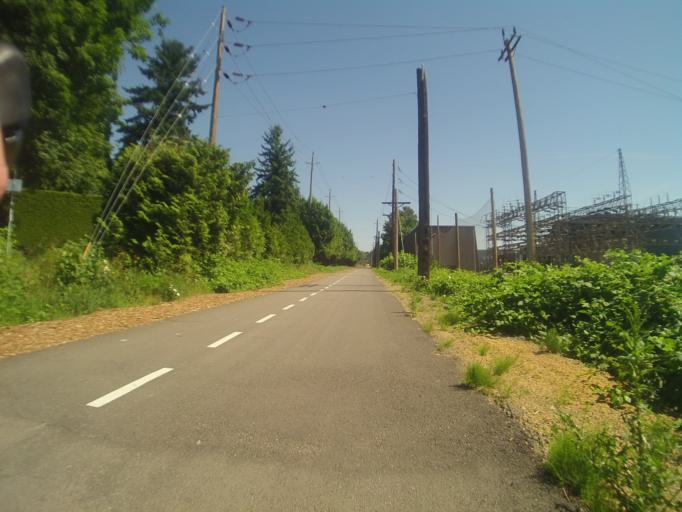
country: CA
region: British Columbia
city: Vancouver
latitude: 49.2505
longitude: -123.1525
